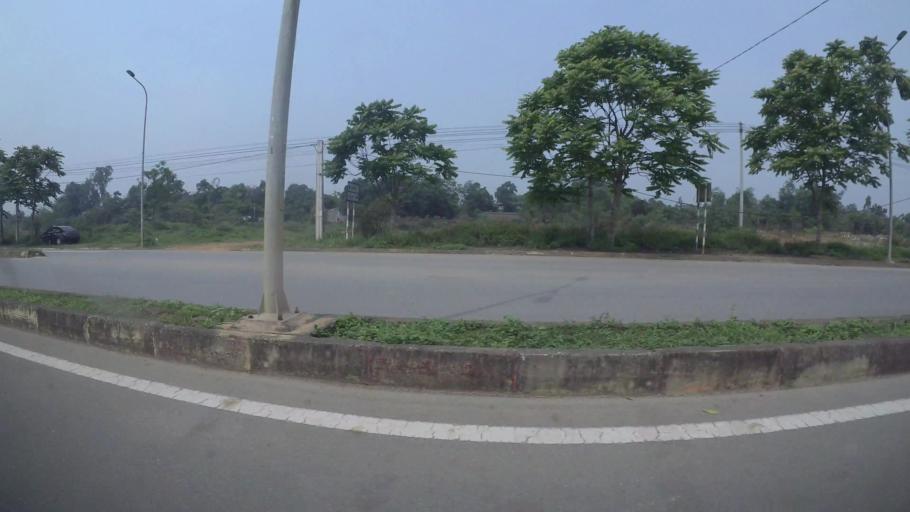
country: VN
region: Ha Noi
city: Lien Quan
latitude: 20.9940
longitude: 105.5353
